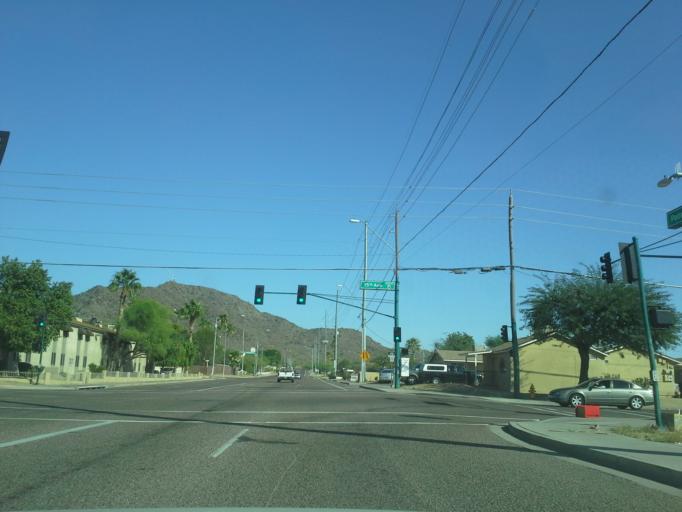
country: US
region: Arizona
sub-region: Maricopa County
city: Glendale
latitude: 33.5820
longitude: -112.0917
